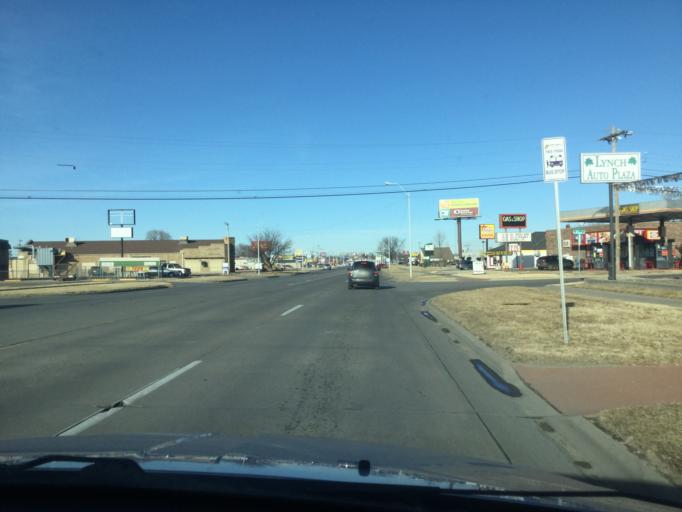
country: US
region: Kansas
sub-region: Shawnee County
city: Topeka
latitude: 39.0819
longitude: -95.6666
